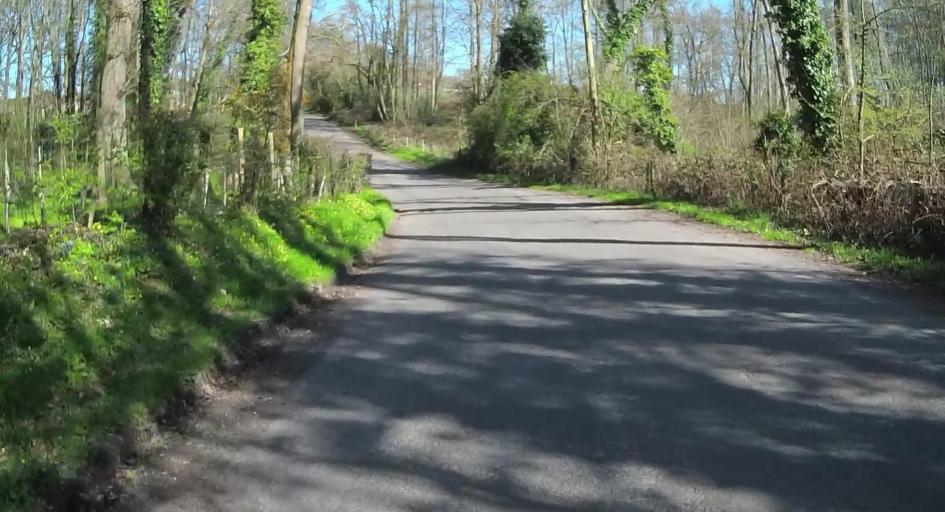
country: GB
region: England
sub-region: West Berkshire
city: Thatcham
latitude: 51.4065
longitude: -1.1954
